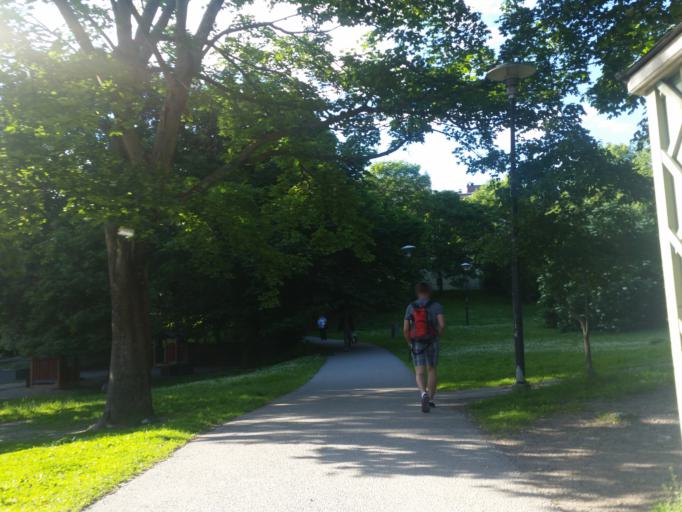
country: SE
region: Stockholm
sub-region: Stockholms Kommun
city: Arsta
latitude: 59.3058
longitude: 18.0823
